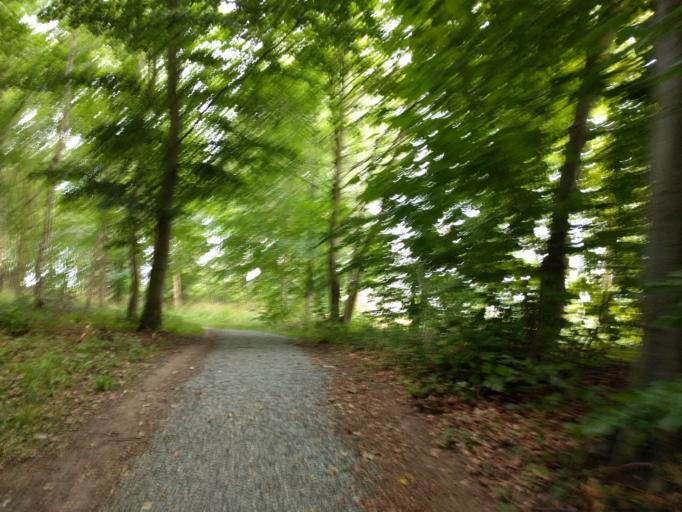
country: DK
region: South Denmark
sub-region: Kerteminde Kommune
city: Munkebo
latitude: 55.4674
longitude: 10.5608
